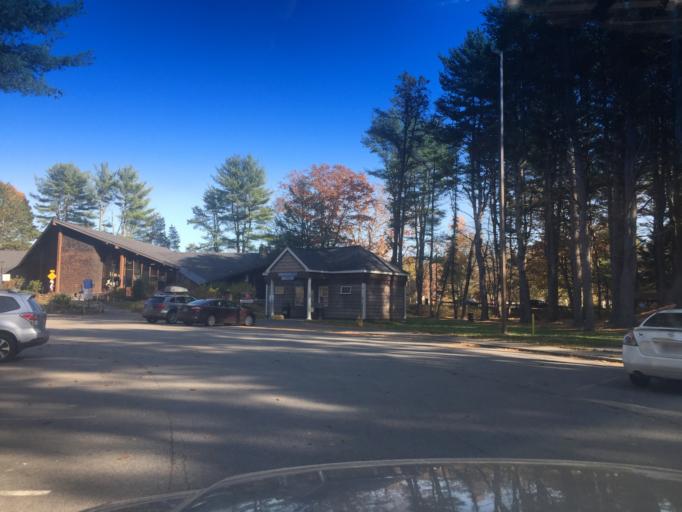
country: US
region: Maine
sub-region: York County
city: Kittery
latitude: 43.1279
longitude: -70.7176
